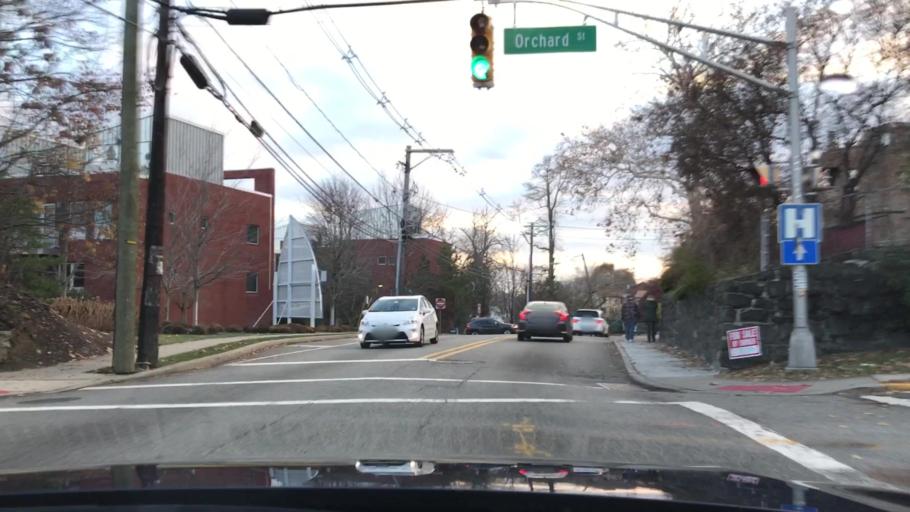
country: US
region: New Jersey
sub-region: Bergen County
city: Fort Lee
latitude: 40.8410
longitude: -73.9696
